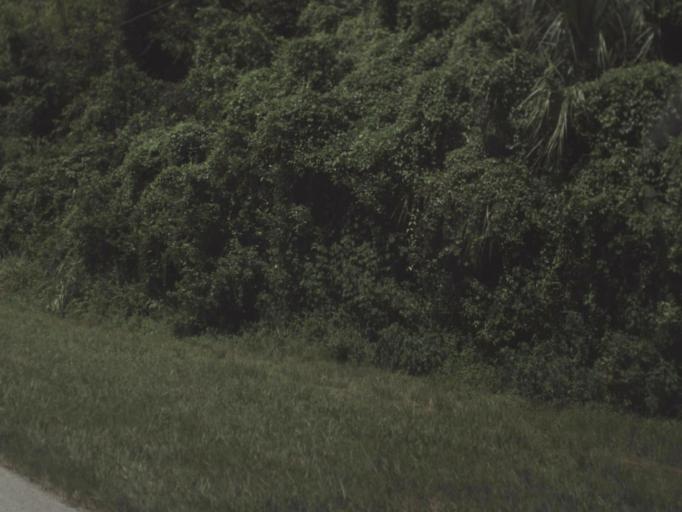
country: US
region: Florida
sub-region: Hillsborough County
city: Thonotosassa
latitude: 28.0677
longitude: -82.3038
